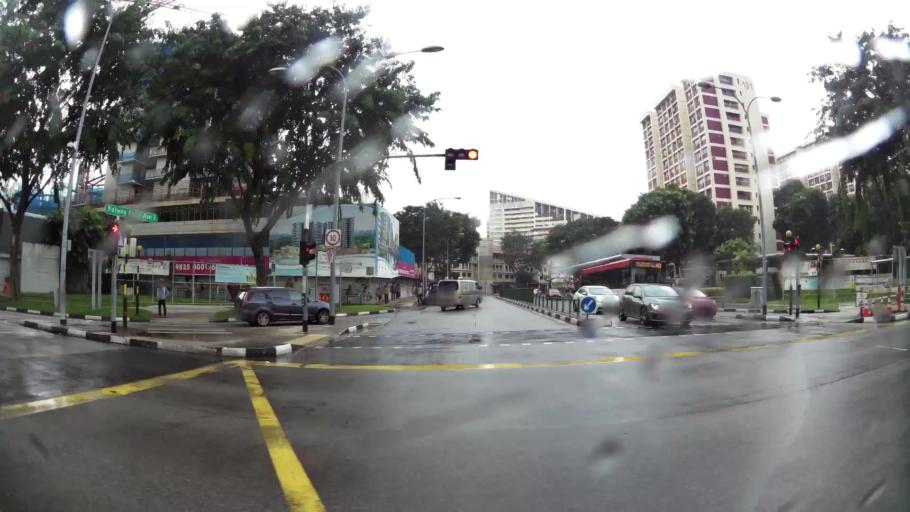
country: SG
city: Singapore
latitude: 1.3323
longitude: 103.8692
